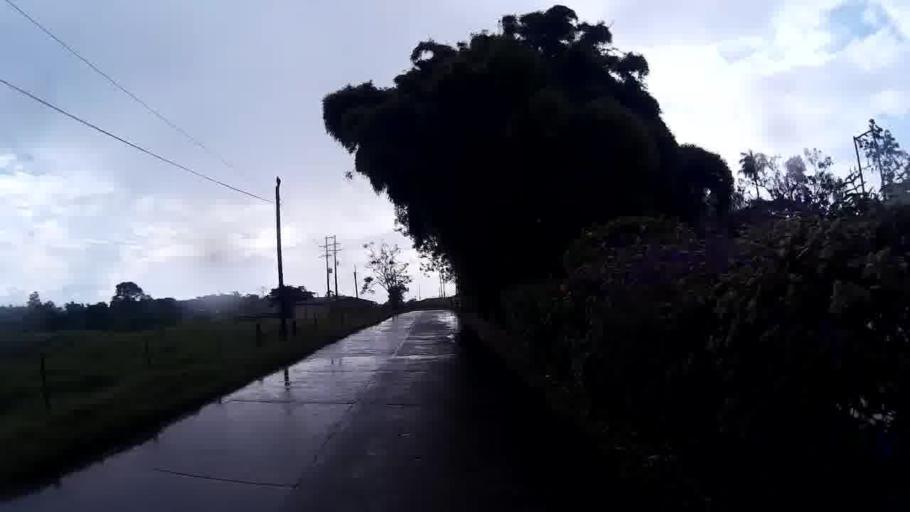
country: CO
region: Quindio
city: Filandia
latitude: 4.6890
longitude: -75.6089
